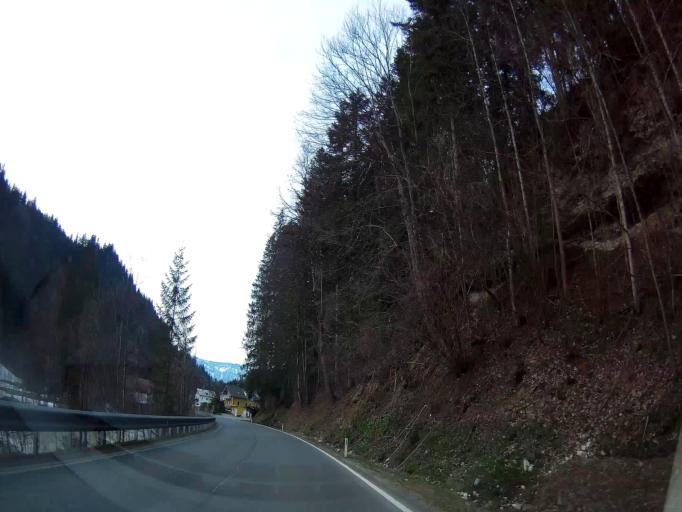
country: AT
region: Salzburg
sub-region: Politischer Bezirk Hallein
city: Abtenau
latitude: 47.5353
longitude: 13.4239
